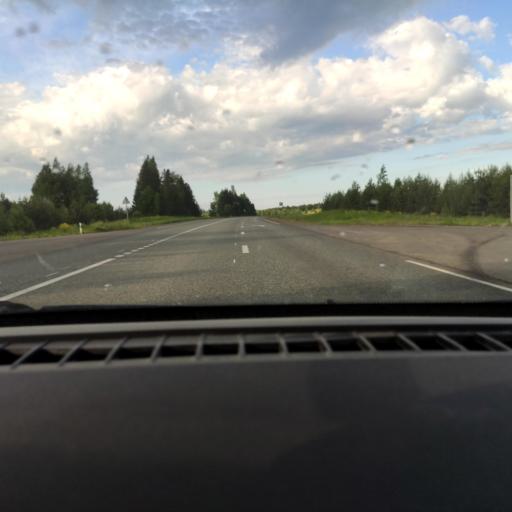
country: RU
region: Udmurtiya
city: Votkinsk
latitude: 57.2510
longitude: 54.2209
